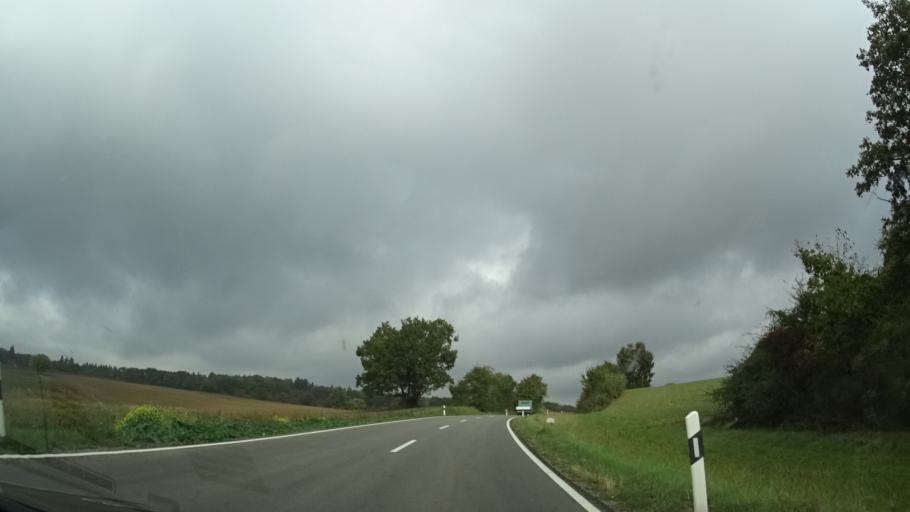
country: DE
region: Baden-Wuerttemberg
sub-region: Karlsruhe Region
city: Konigsbach-Stein
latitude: 48.9806
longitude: 8.6384
